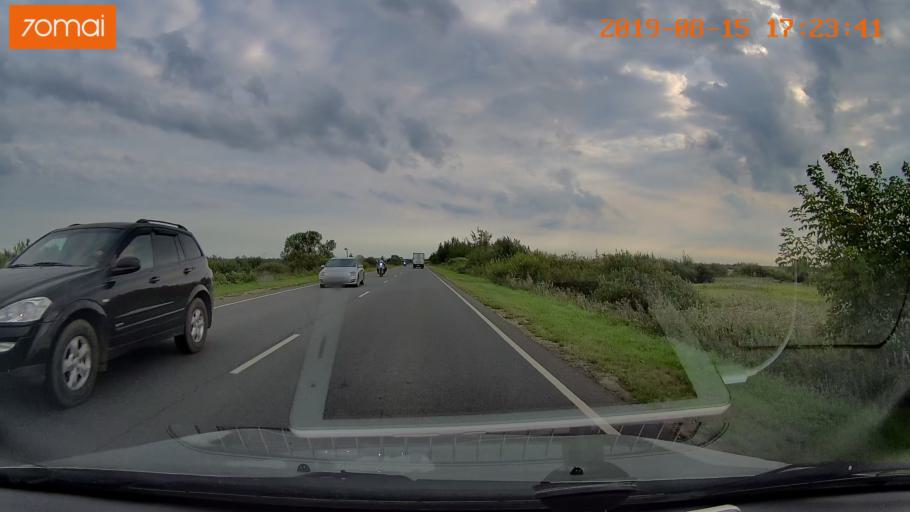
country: RU
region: Moskovskaya
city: Ashitkovo
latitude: 55.3981
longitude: 38.5548
